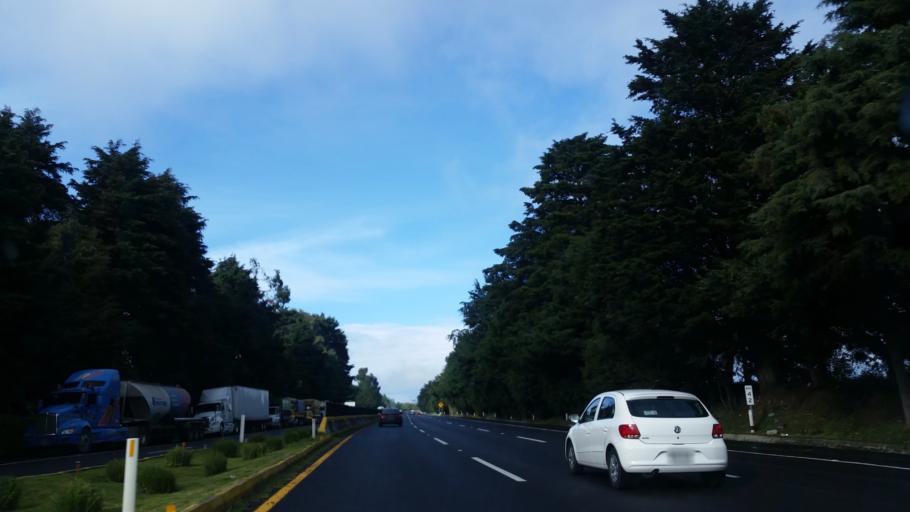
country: MX
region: Morelos
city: Tres Marias
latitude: 19.1258
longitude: -99.1763
